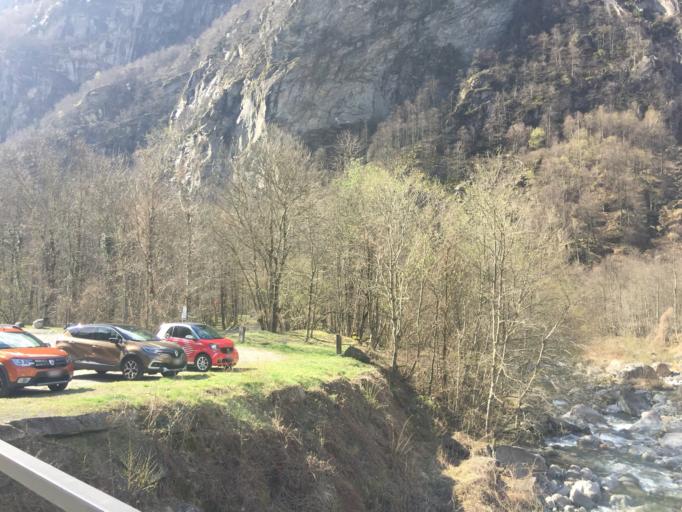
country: CH
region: Ticino
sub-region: Vallemaggia District
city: Cevio
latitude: 46.3735
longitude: 8.5479
